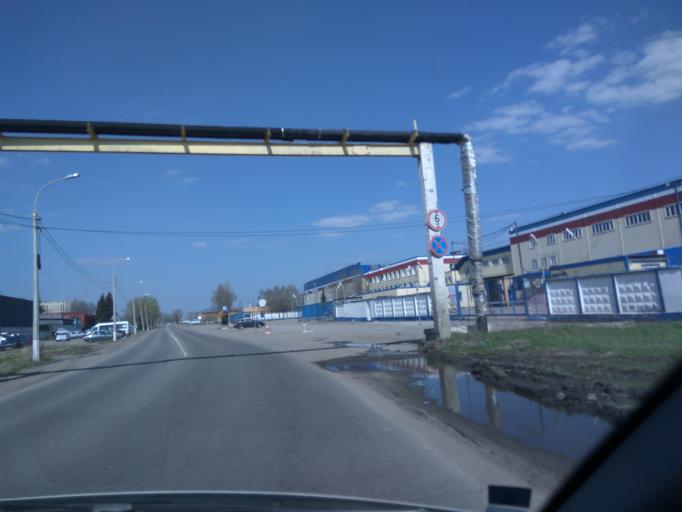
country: RU
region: Moskovskaya
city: Ramenskoye
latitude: 55.5614
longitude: 38.2636
